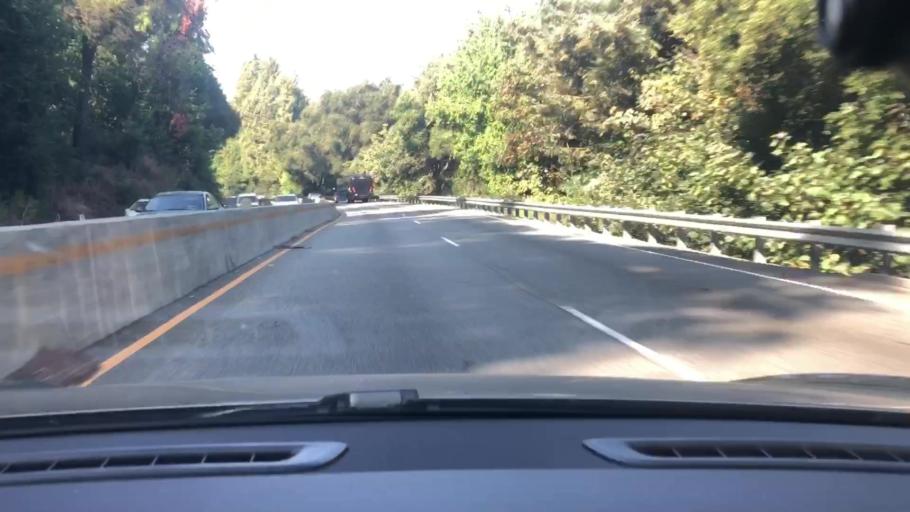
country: US
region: California
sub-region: Santa Clara County
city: Lexington Hills
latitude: 37.1476
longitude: -121.9868
